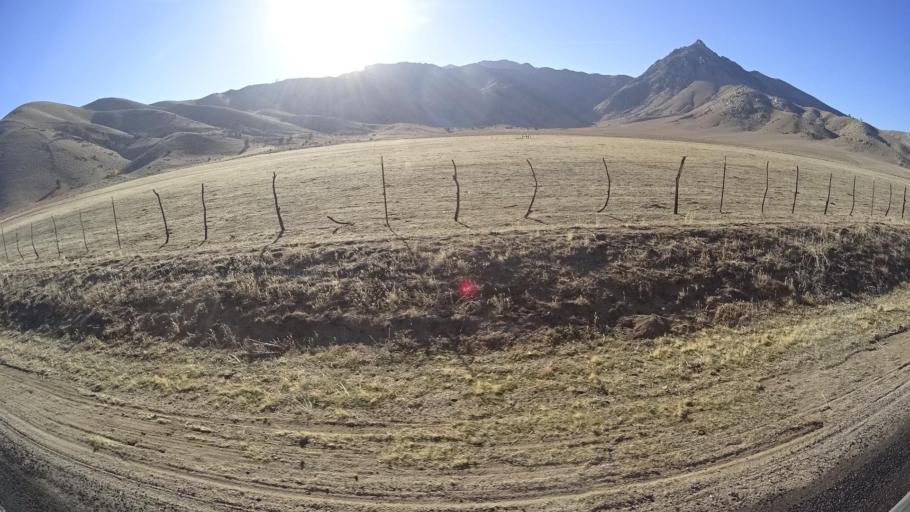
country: US
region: California
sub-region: Kern County
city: Weldon
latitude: 35.6202
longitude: -118.2546
